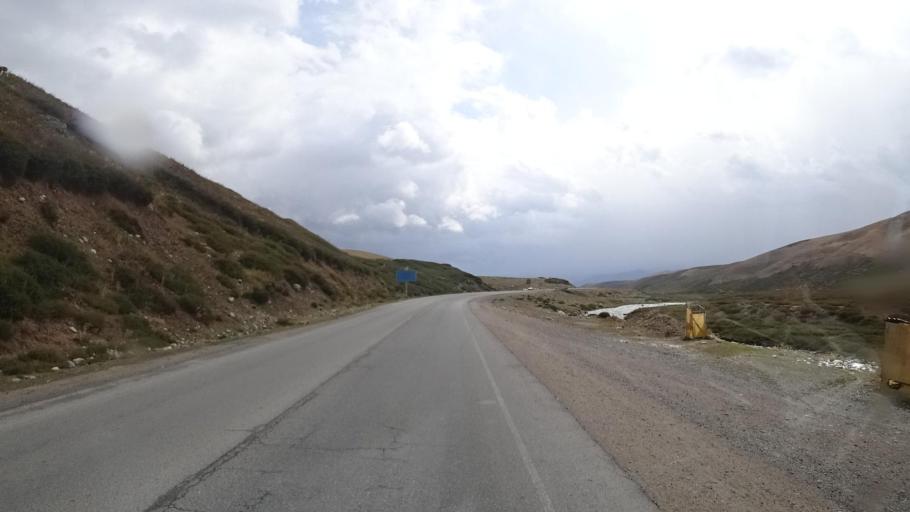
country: KG
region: Jalal-Abad
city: Uch-Terek
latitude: 42.2085
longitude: 73.2599
